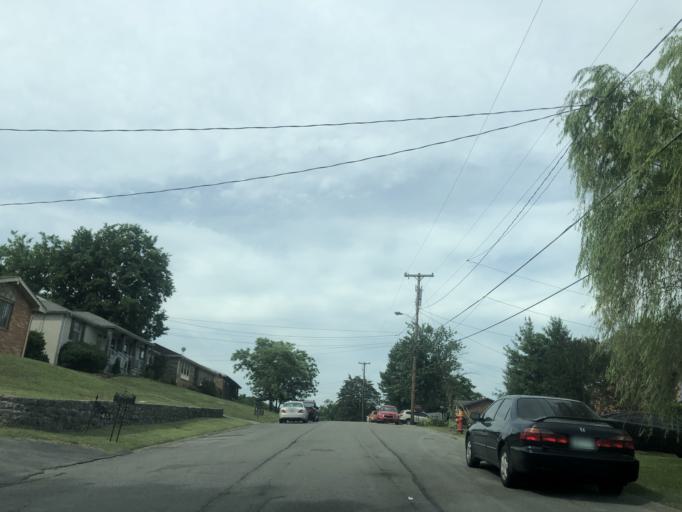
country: US
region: Tennessee
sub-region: Davidson County
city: Nashville
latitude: 36.2224
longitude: -86.8141
